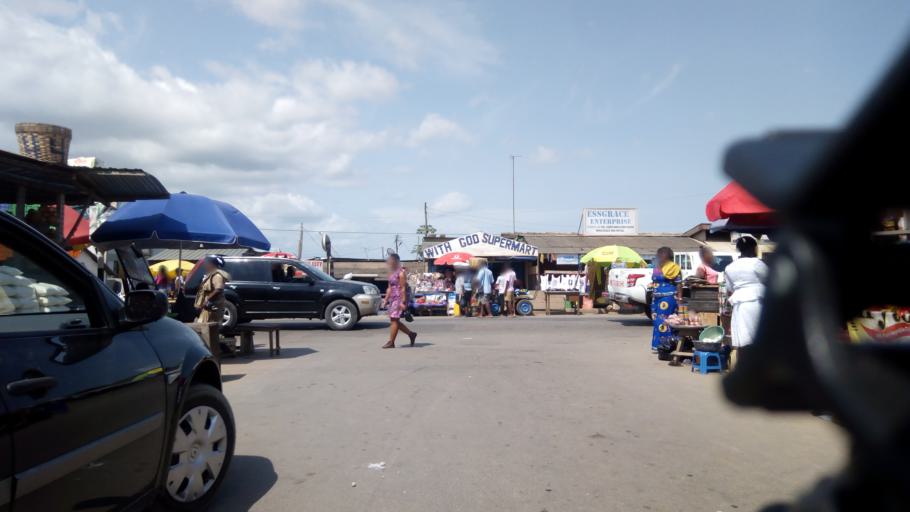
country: GH
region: Central
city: Cape Coast
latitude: 5.1331
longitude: -1.2766
